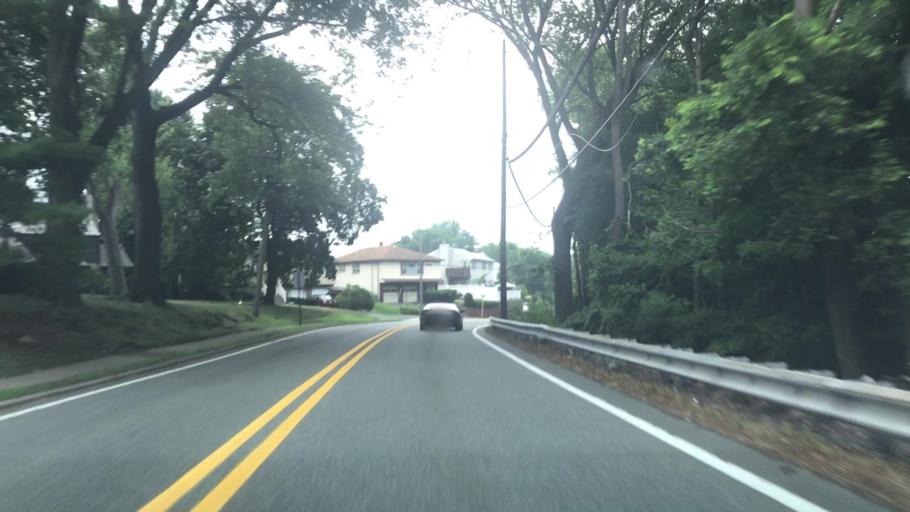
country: US
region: New Jersey
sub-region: Bergen County
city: Elmwood Park
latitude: 40.9165
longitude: -74.1303
